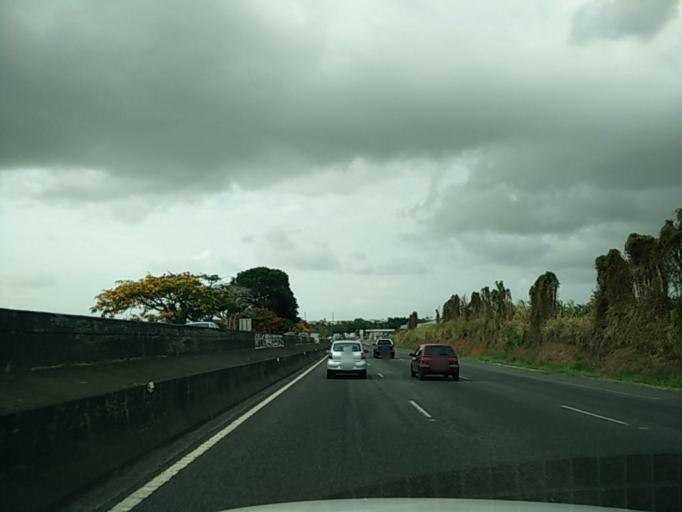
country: GP
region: Guadeloupe
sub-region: Guadeloupe
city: Petit-Bourg
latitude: 16.2282
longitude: -61.5928
